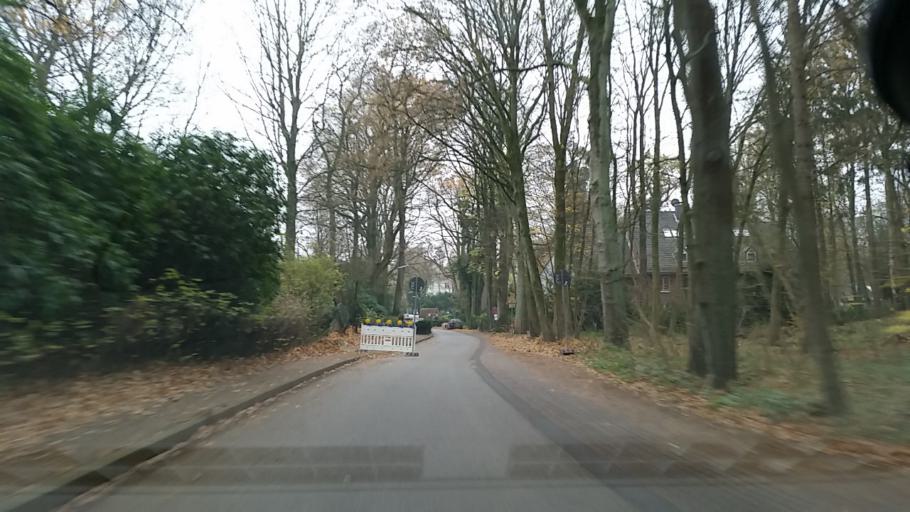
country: DE
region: Schleswig-Holstein
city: Rellingen
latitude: 53.5726
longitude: 9.7895
